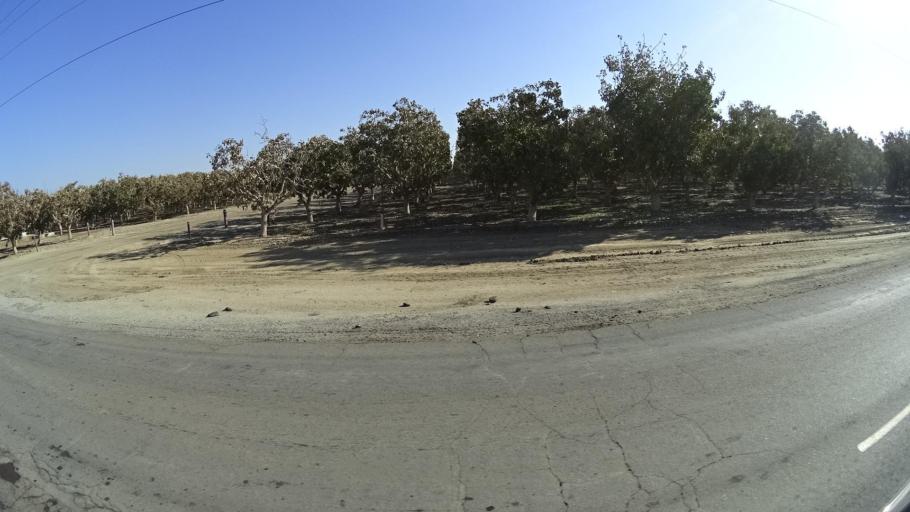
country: US
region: California
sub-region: Kern County
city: McFarland
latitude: 35.7249
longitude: -119.2051
